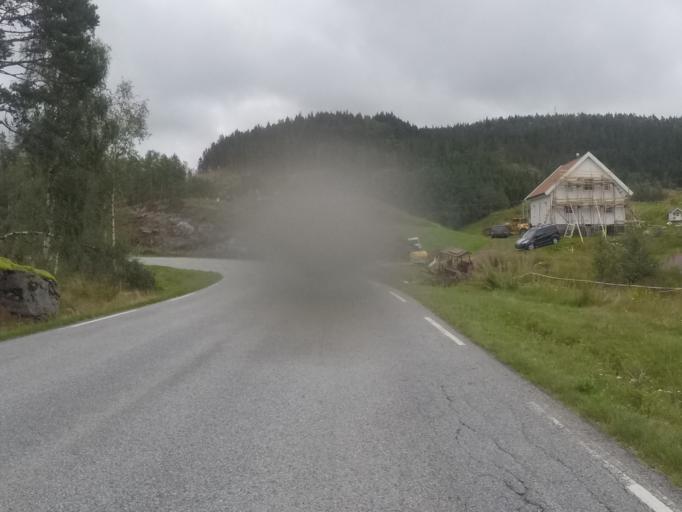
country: NO
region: Vest-Agder
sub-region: Audnedal
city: Konsmo
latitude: 58.2780
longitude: 7.3898
